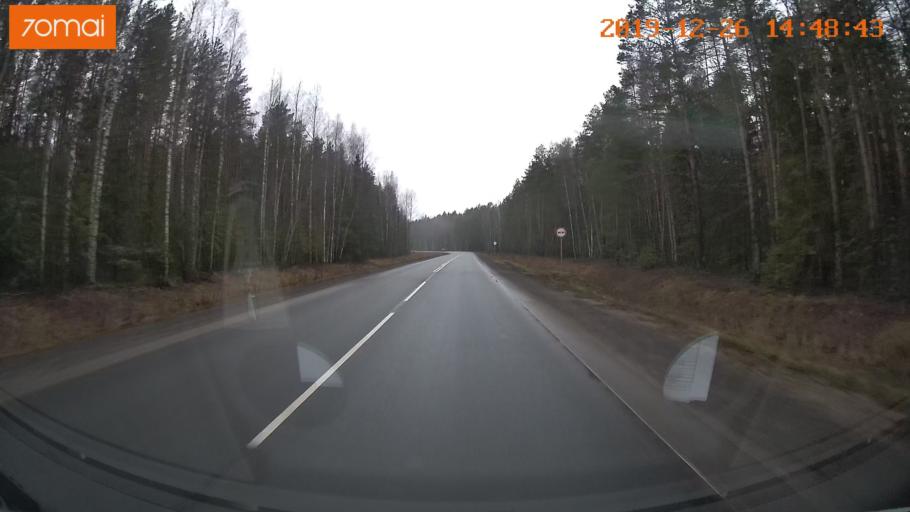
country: RU
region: Jaroslavl
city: Poshekhon'ye
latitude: 58.3422
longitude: 38.9664
